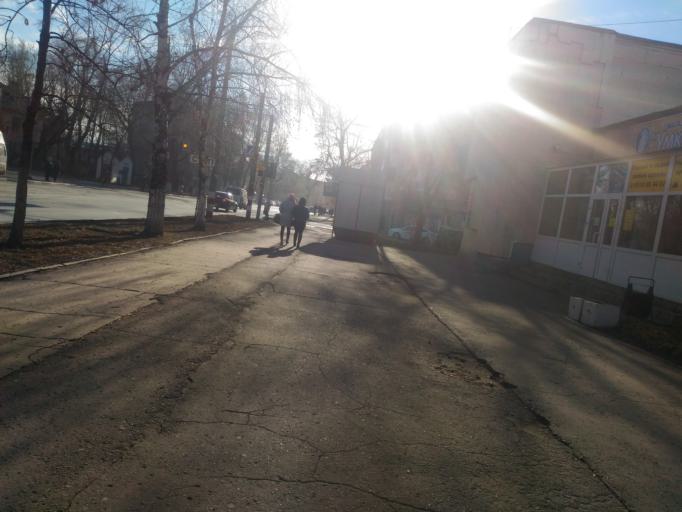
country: RU
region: Ulyanovsk
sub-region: Ulyanovskiy Rayon
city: Ulyanovsk
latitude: 54.3250
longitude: 48.3884
